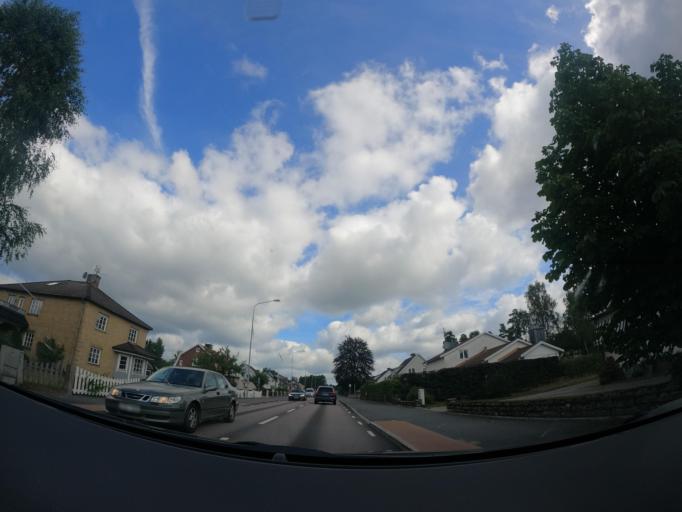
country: SE
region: Joenkoeping
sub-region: Gislaveds Kommun
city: Smalandsstenar
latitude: 57.1708
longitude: 13.4189
